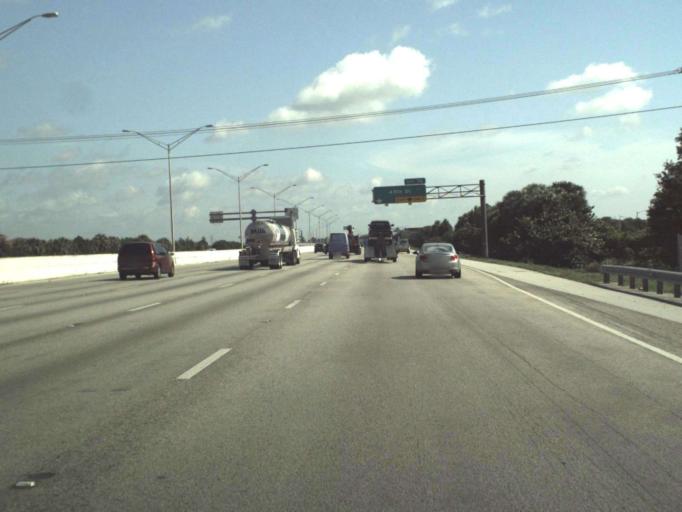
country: US
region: Florida
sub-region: Palm Beach County
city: Mangonia Park
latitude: 26.7493
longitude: -80.0900
